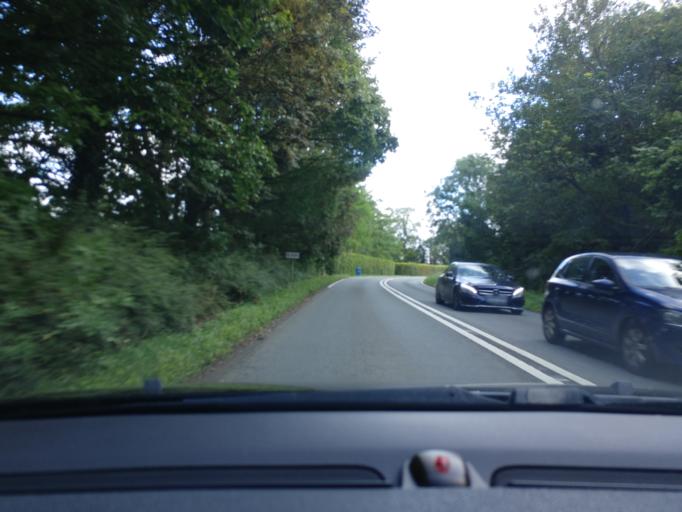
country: GB
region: England
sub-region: Oxfordshire
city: Somerton
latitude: 51.9064
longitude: -1.2243
